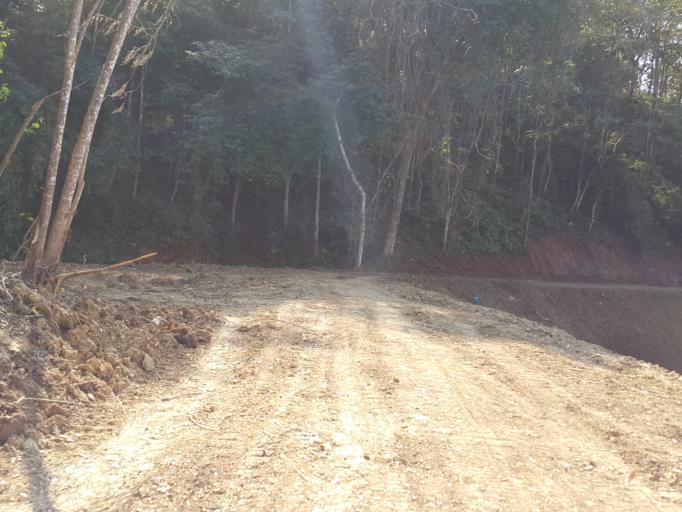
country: TH
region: Chiang Mai
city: Mae On
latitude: 18.8346
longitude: 99.2372
